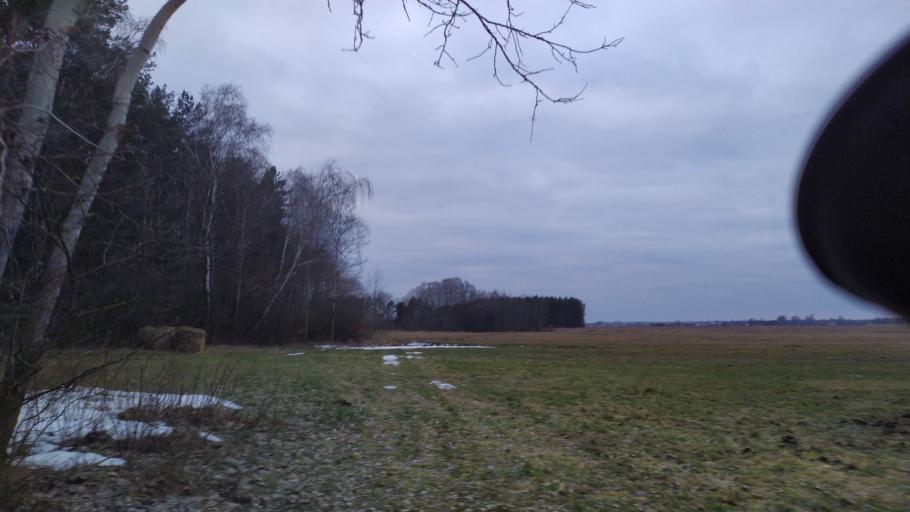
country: PL
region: Lublin Voivodeship
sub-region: Powiat lubartowski
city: Abramow
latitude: 51.4300
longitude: 22.2923
